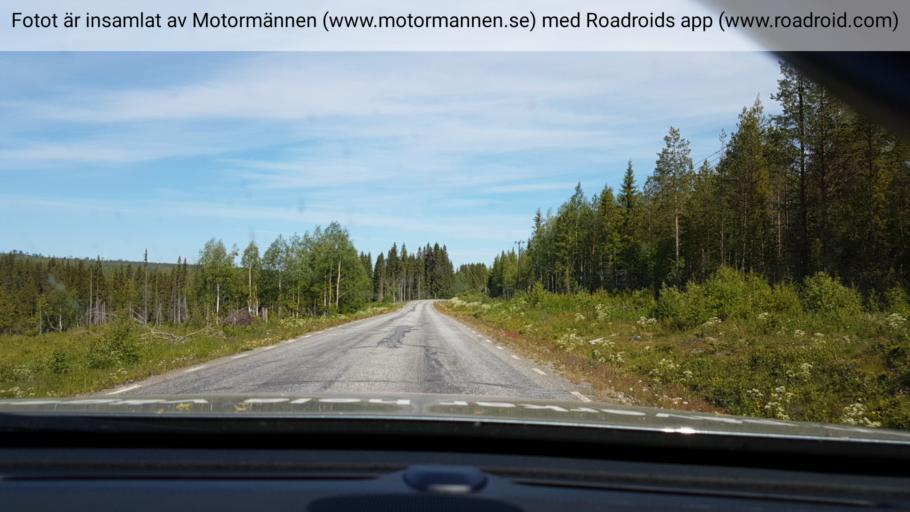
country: SE
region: Vaesterbotten
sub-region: Vilhelmina Kommun
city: Sjoberg
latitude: 64.5365
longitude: 15.8897
